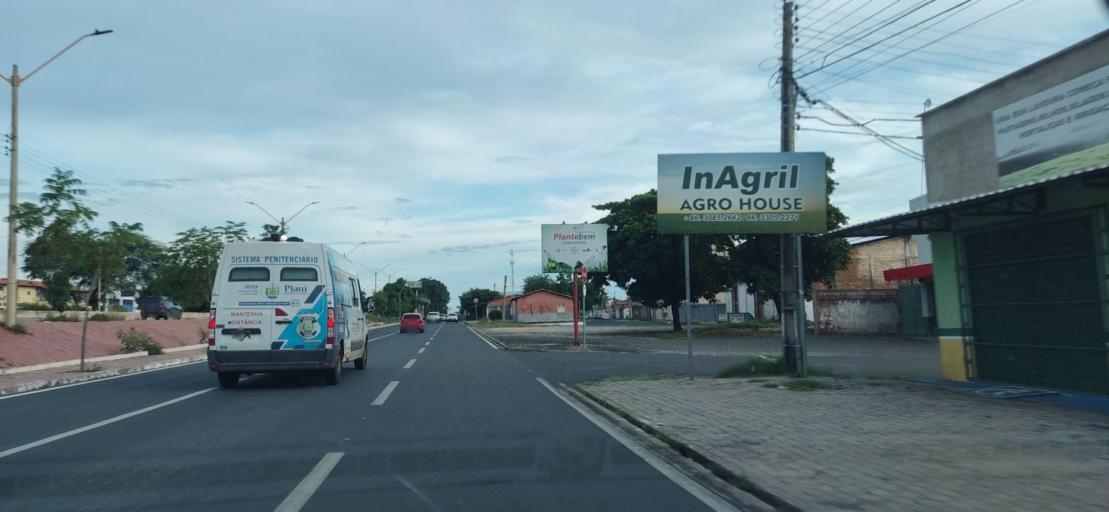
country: BR
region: Piaui
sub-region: Teresina
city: Teresina
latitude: -5.1325
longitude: -42.7913
